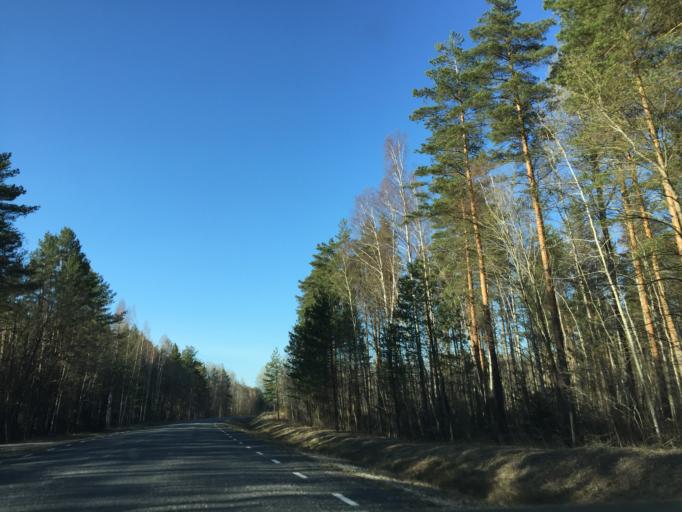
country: RU
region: Pskov
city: Gdov
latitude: 59.0538
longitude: 27.7018
